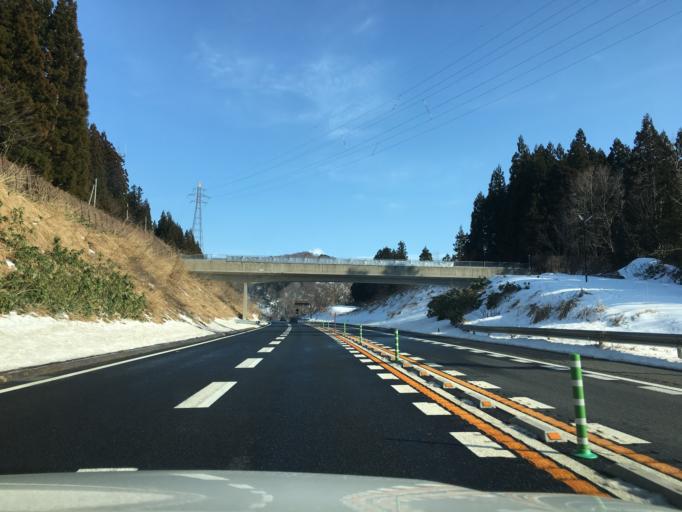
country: JP
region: Yamagata
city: Tsuruoka
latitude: 38.5905
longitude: 139.8883
